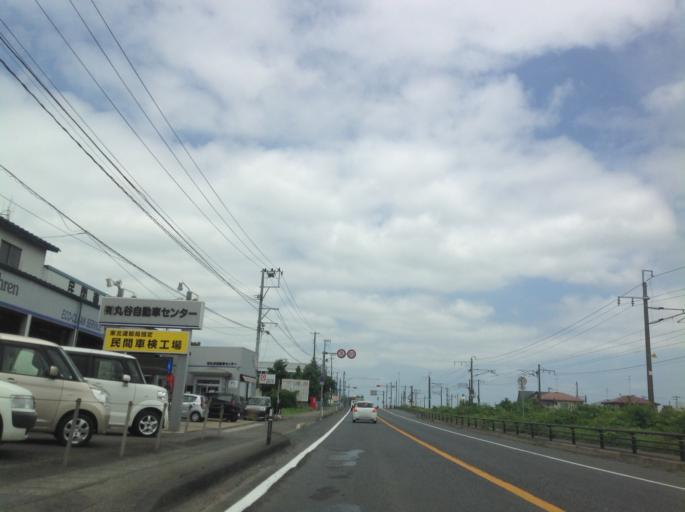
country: JP
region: Iwate
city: Mizusawa
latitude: 39.1183
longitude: 141.1464
